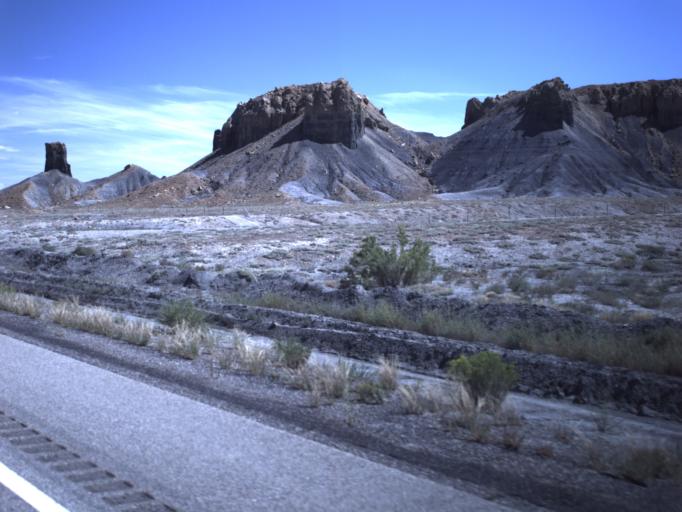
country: US
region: Utah
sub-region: Emery County
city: Ferron
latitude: 38.8103
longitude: -111.2186
